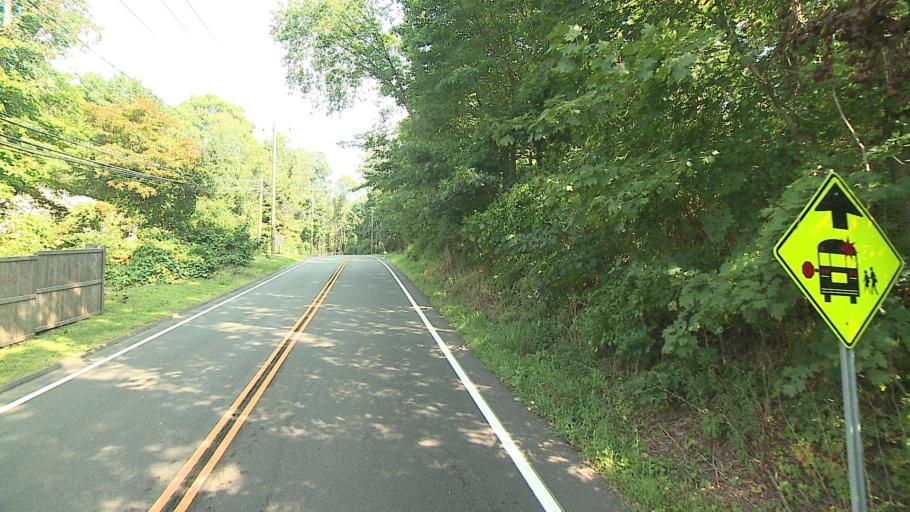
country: US
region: Connecticut
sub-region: Fairfield County
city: Wilton
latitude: 41.2184
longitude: -73.3942
